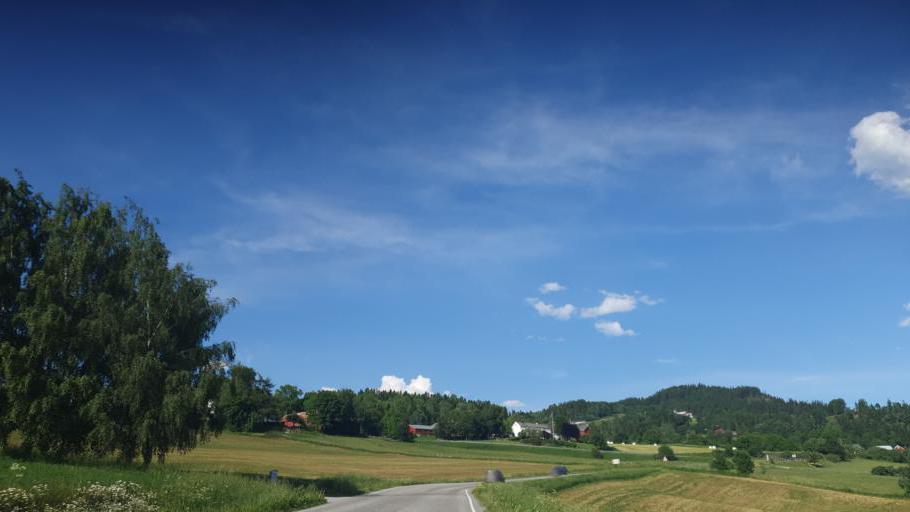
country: NO
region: Nord-Trondelag
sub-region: Leksvik
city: Leksvik
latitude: 63.6752
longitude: 10.6333
